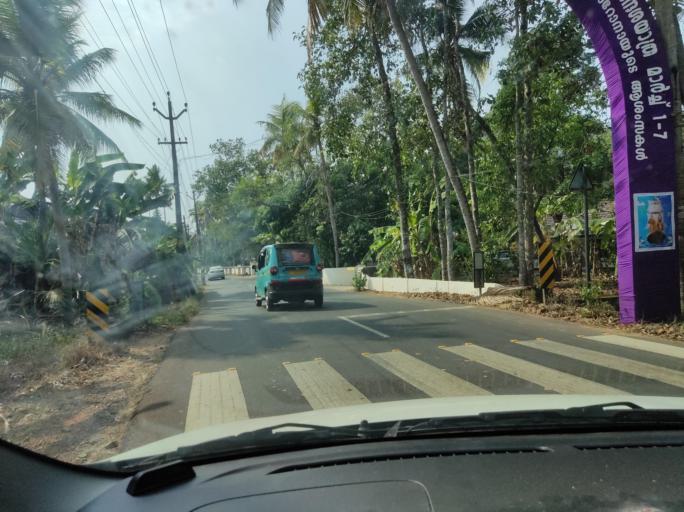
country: IN
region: Kerala
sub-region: Kottayam
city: Kottayam
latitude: 9.6885
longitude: 76.5010
